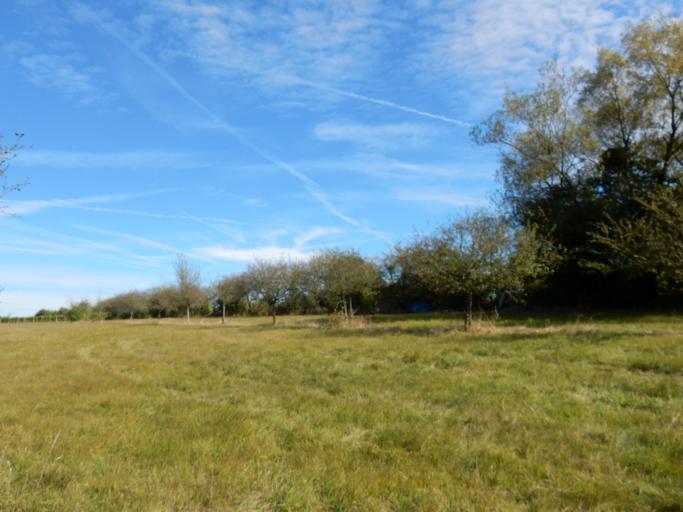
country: LU
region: Grevenmacher
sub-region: Canton de Grevenmacher
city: Wormeldange
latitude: 49.6049
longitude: 6.3945
